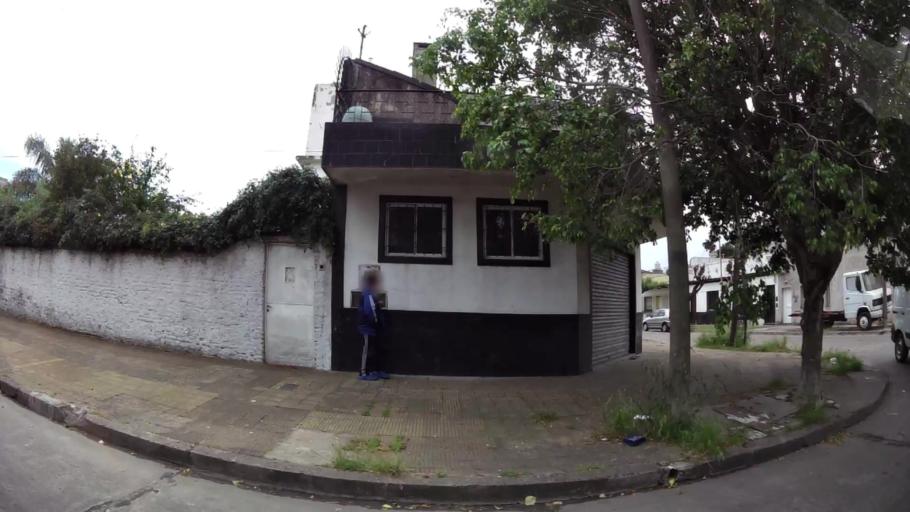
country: AR
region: Buenos Aires
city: San Justo
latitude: -34.6676
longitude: -58.5480
